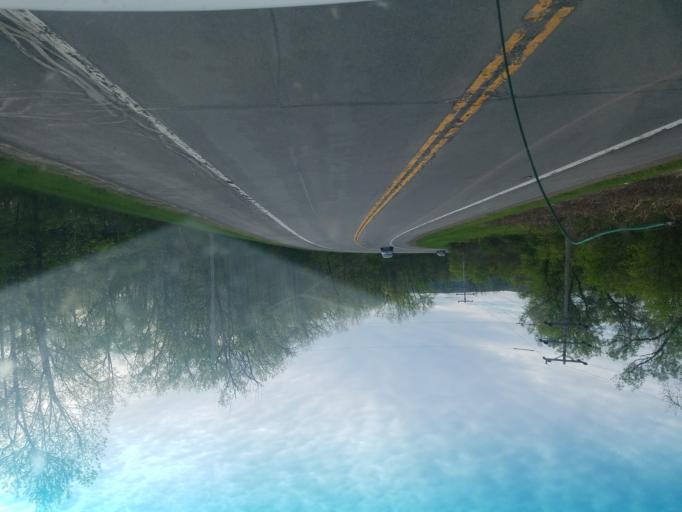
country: US
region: New York
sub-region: Herkimer County
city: Little Falls
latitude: 43.0263
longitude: -74.8743
